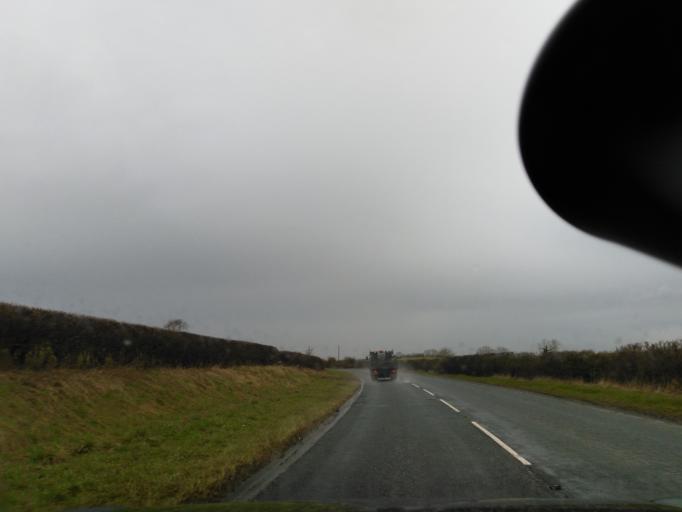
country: GB
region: England
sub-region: North Yorkshire
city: Northallerton
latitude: 54.3152
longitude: -1.4084
